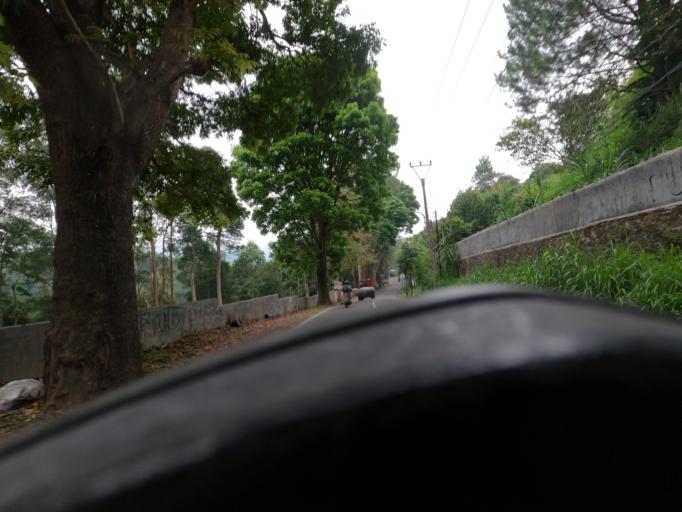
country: ID
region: West Java
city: Lembang
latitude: -6.8009
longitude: 107.5769
